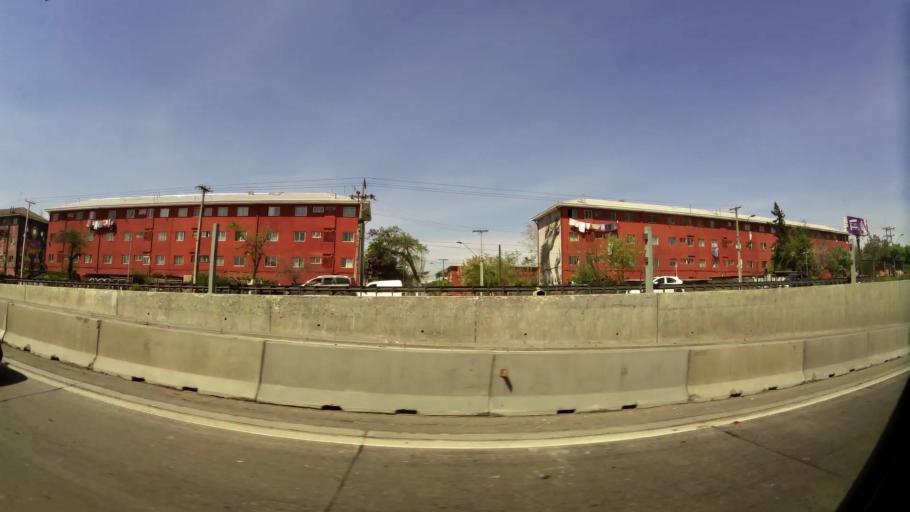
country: CL
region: Santiago Metropolitan
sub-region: Provincia de Santiago
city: Santiago
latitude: -33.4997
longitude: -70.6659
